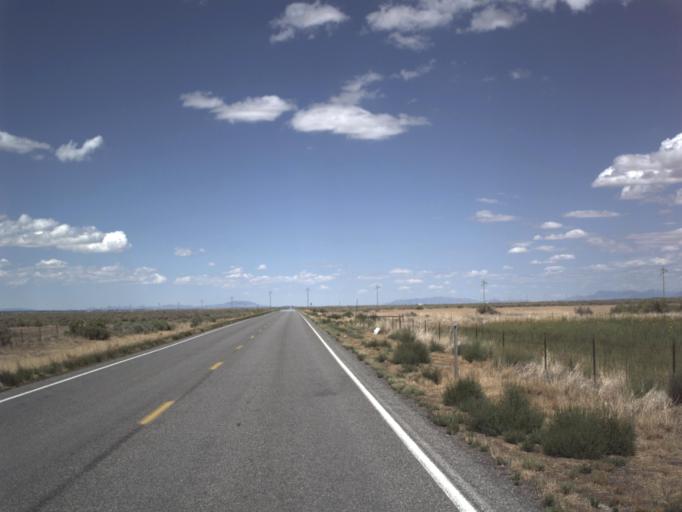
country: US
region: Utah
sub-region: Millard County
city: Delta
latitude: 39.2169
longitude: -112.4183
